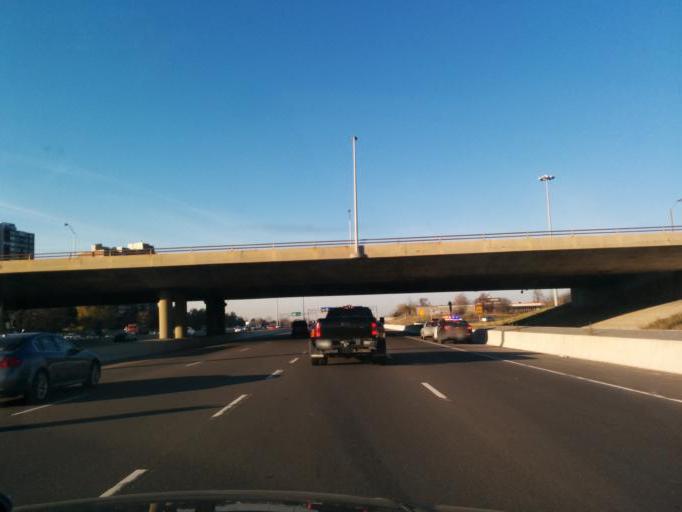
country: CA
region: Ontario
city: Etobicoke
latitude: 43.6537
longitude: -79.5667
